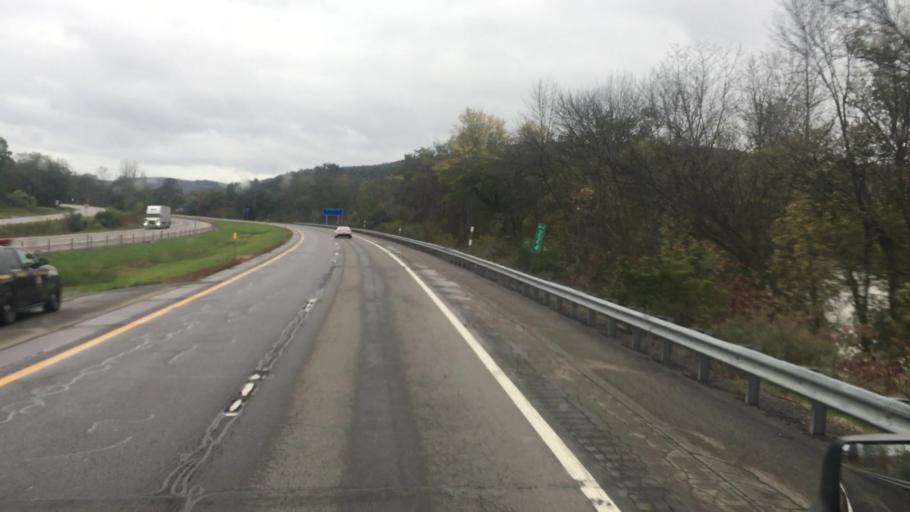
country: US
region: New York
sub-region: Tioga County
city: Owego
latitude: 42.0991
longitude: -76.2404
